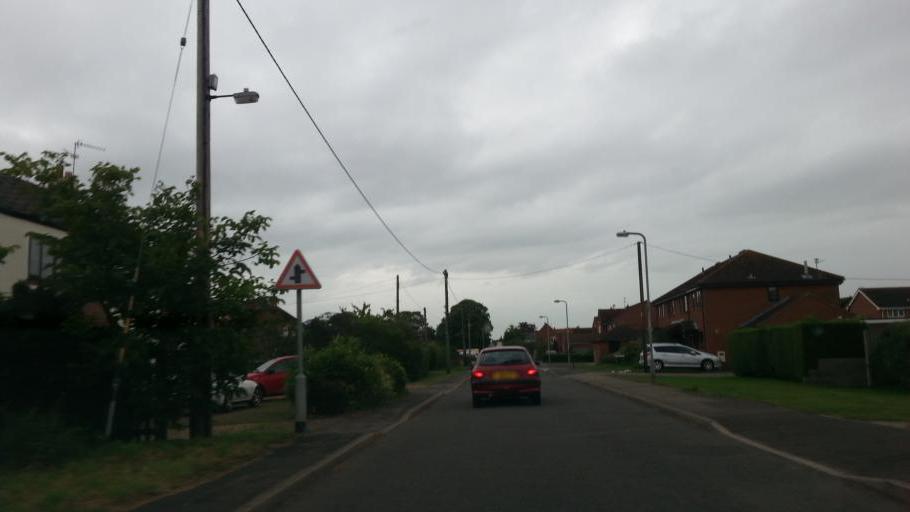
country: GB
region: England
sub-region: Lincolnshire
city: Long Bennington
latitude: 53.0298
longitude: -0.7350
